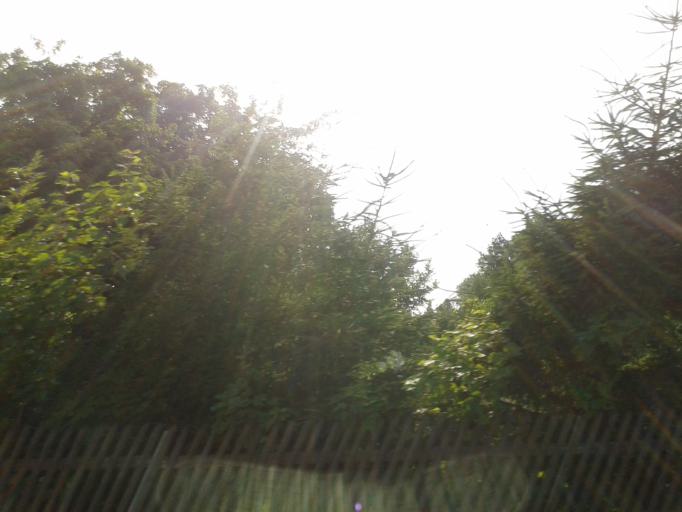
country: DE
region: Saxony
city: Halsbrucke
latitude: 50.9799
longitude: 13.3278
